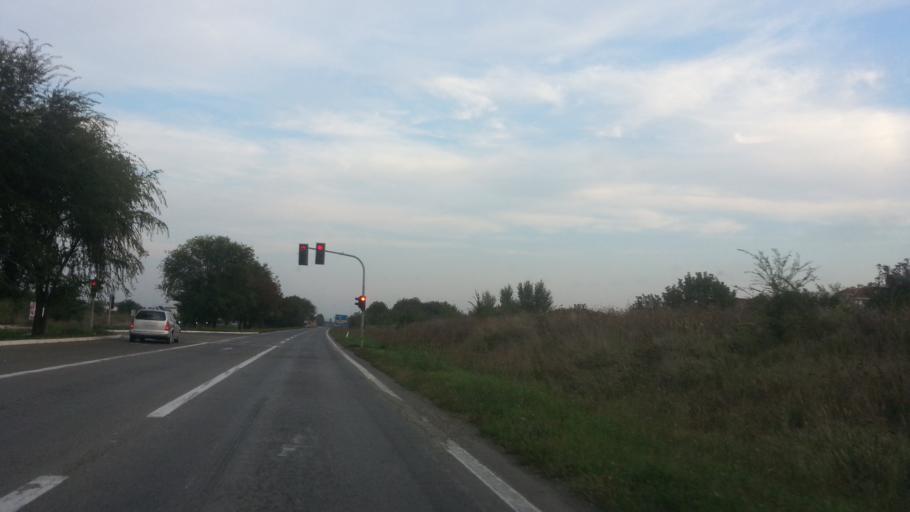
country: RS
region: Central Serbia
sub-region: Belgrade
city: Zemun
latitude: 44.8750
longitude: 20.3296
